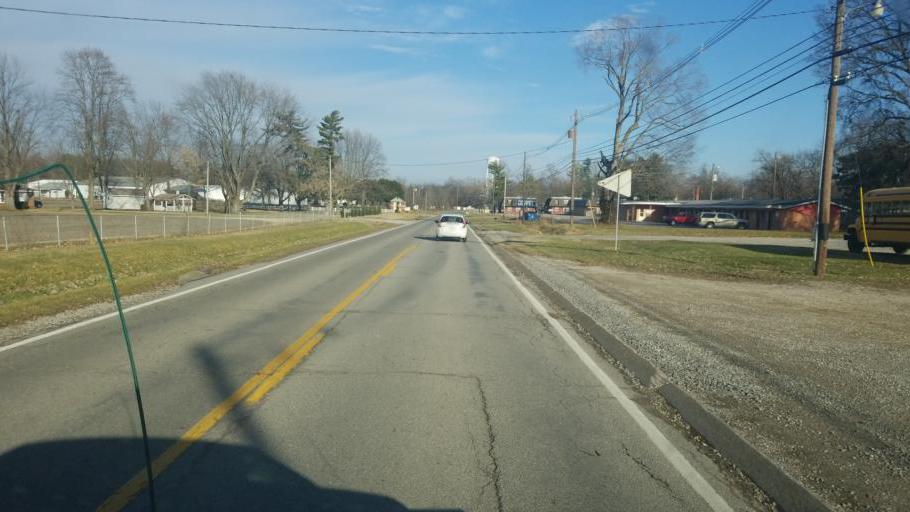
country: US
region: Illinois
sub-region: Wabash County
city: Mount Carmel
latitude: 38.4012
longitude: -87.7841
